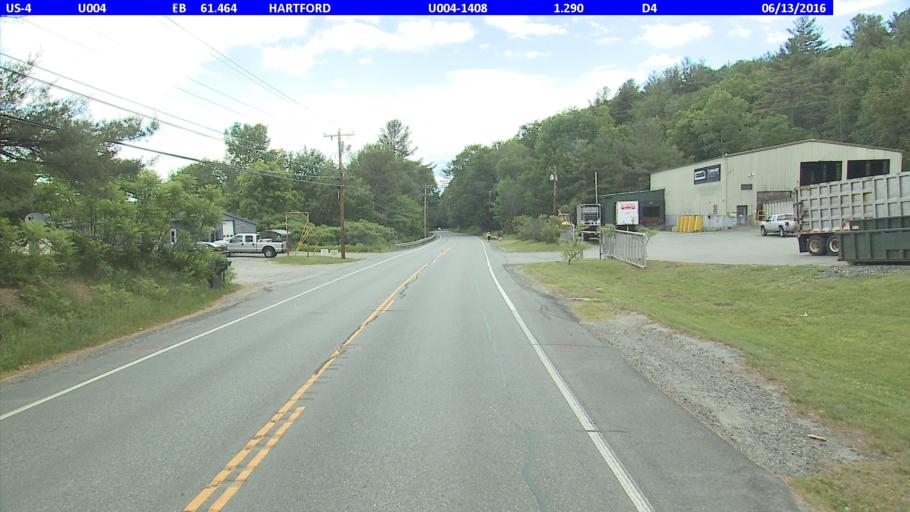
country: US
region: Vermont
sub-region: Windsor County
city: White River Junction
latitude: 43.6617
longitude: -72.3566
